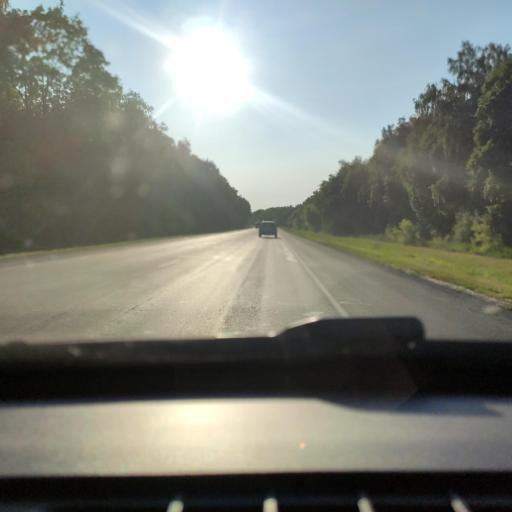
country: RU
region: Voronezj
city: Kashirskoye
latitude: 51.4876
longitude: 39.6435
